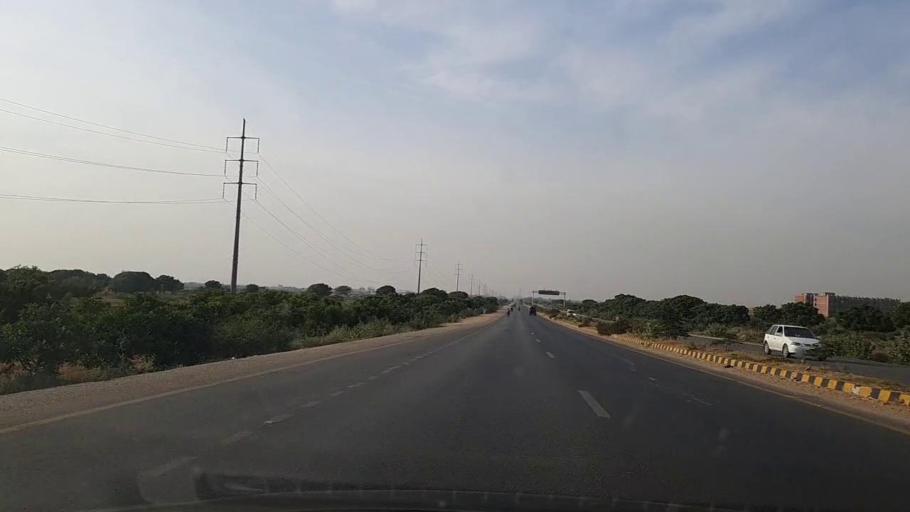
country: PK
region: Sindh
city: Gharo
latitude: 24.7689
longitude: 67.5490
